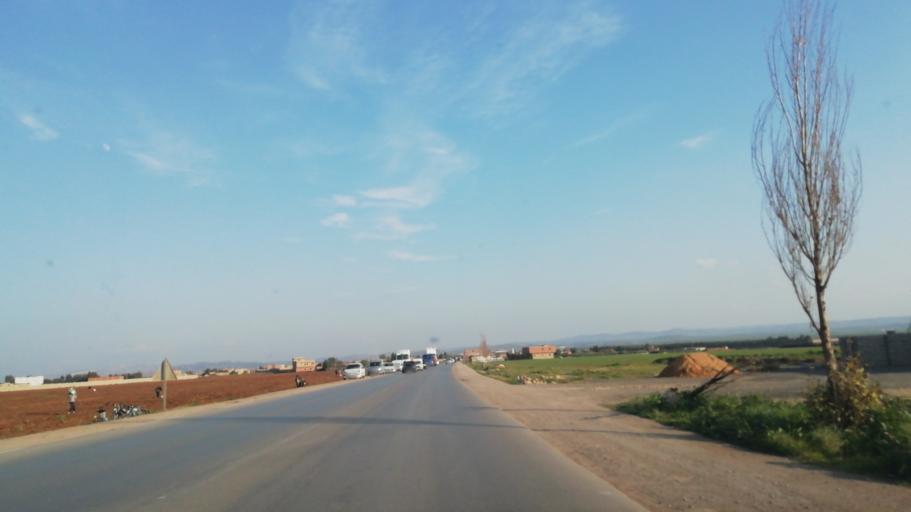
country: DZ
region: Relizane
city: Djidiouia
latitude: 35.8984
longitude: 0.6854
